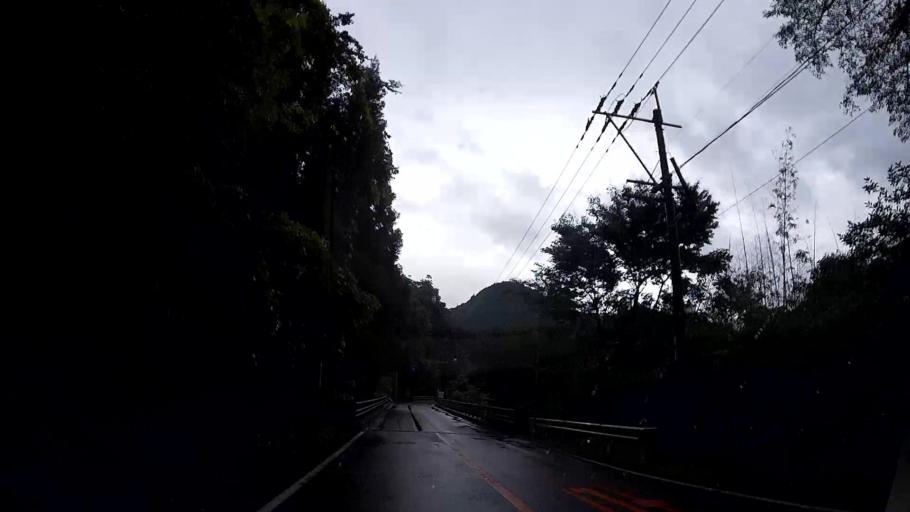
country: JP
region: Oita
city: Hita
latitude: 33.1817
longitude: 131.0033
